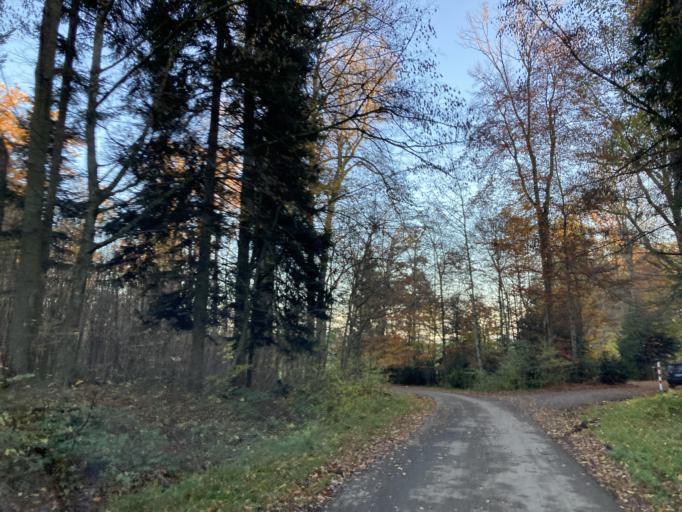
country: DE
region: Baden-Wuerttemberg
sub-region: Tuebingen Region
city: Hirrlingen
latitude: 48.4384
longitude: 8.8936
